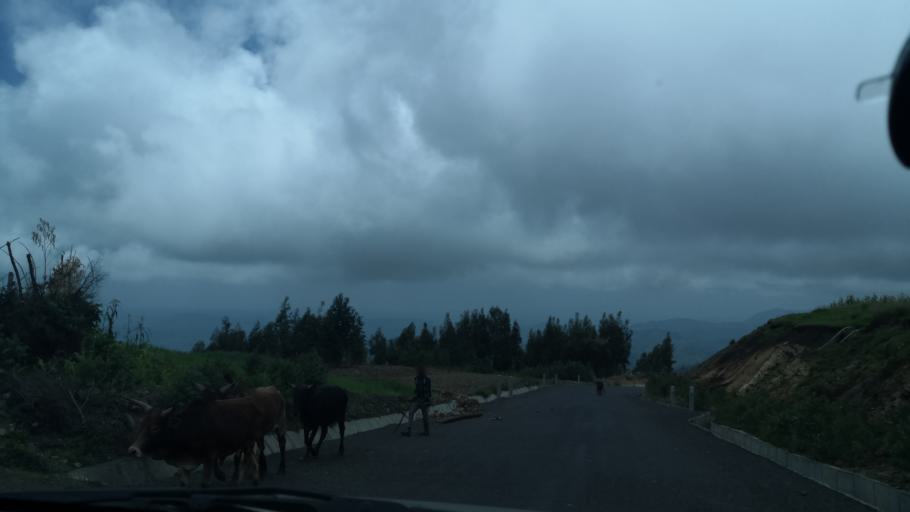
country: ET
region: Amhara
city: Abomsa
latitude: 10.3347
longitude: 39.8406
